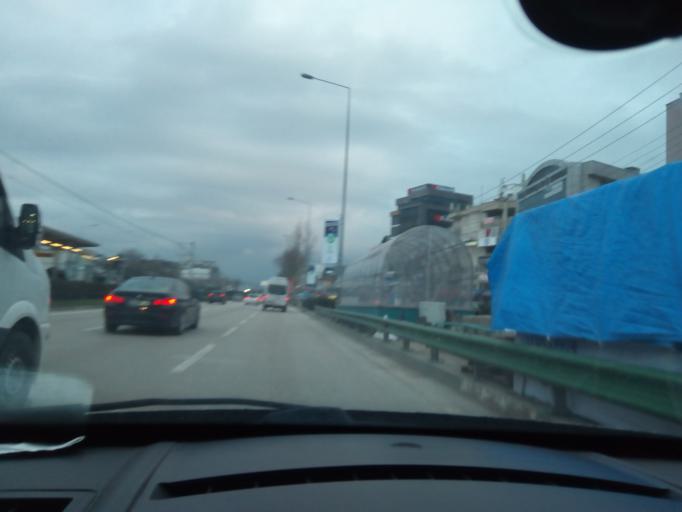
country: TR
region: Bursa
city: Niluefer
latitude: 40.2369
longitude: 28.9753
